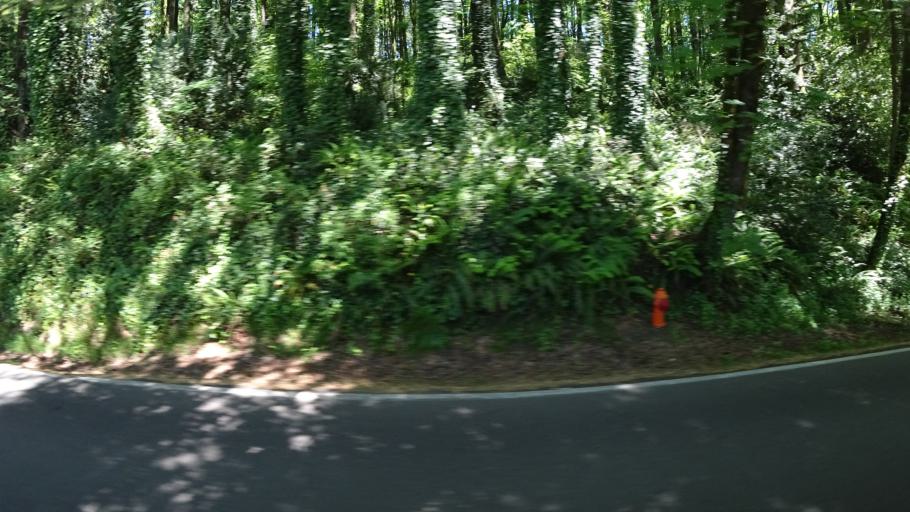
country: US
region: Oregon
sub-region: Multnomah County
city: Portland
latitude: 45.4989
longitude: -122.7111
